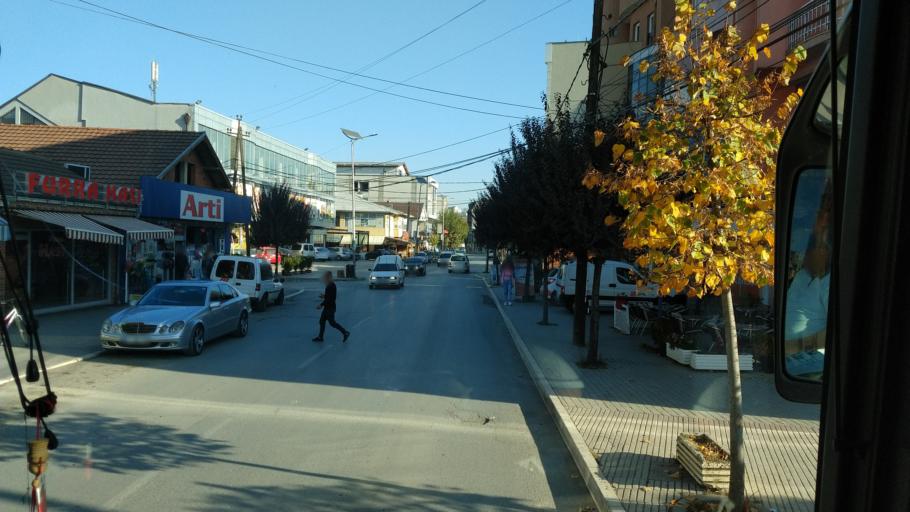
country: XK
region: Ferizaj
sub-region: Komuna e Shtimes
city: Shtime
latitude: 42.4339
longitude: 21.0372
